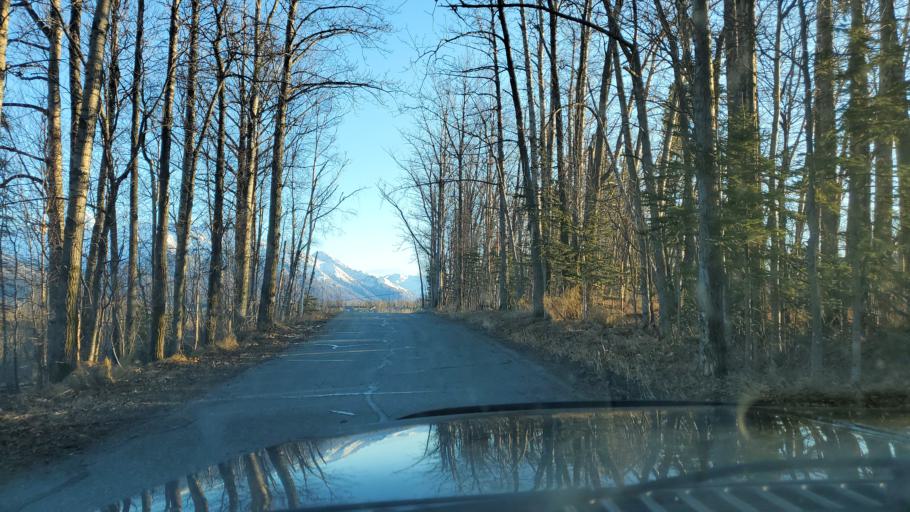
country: US
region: Alaska
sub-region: Matanuska-Susitna Borough
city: Palmer
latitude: 61.5989
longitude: -149.1440
